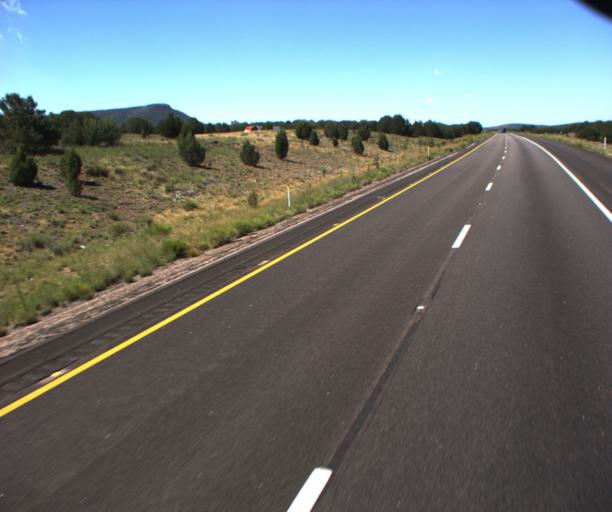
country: US
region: Arizona
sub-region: Mohave County
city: Peach Springs
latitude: 35.2248
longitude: -113.2391
